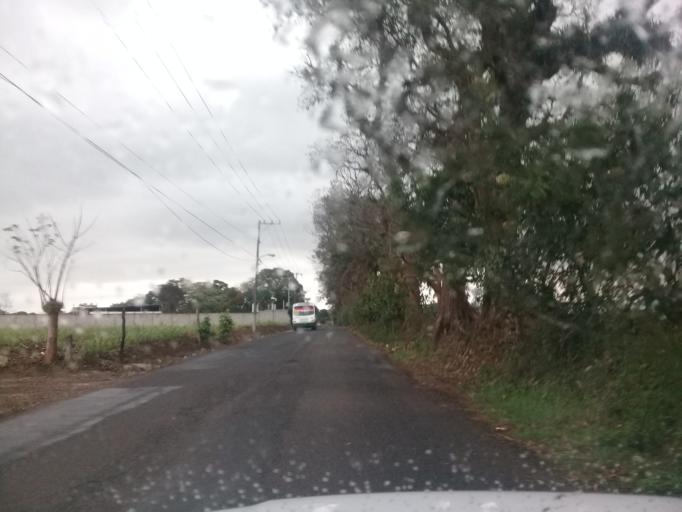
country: MX
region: Veracruz
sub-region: Cordoba
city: Veinte de Noviembre
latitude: 18.8570
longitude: -96.9512
